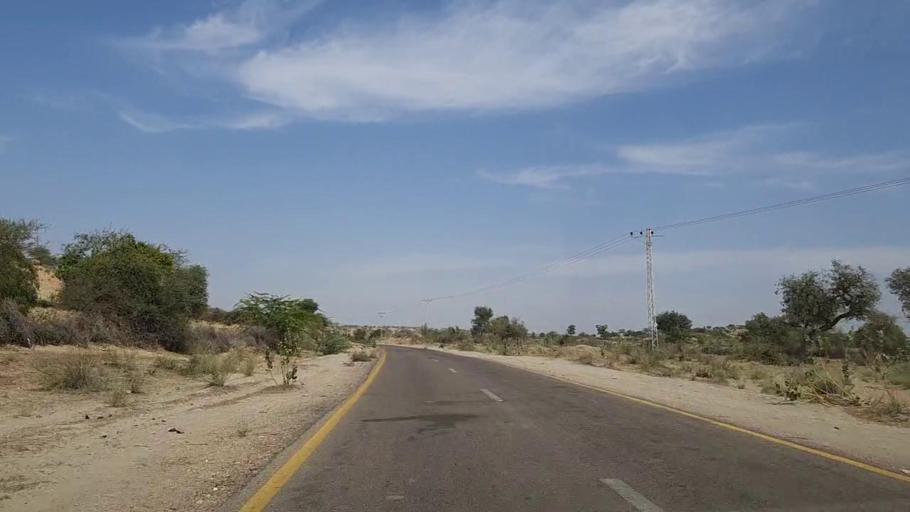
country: PK
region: Sindh
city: Mithi
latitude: 24.7942
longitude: 69.8148
